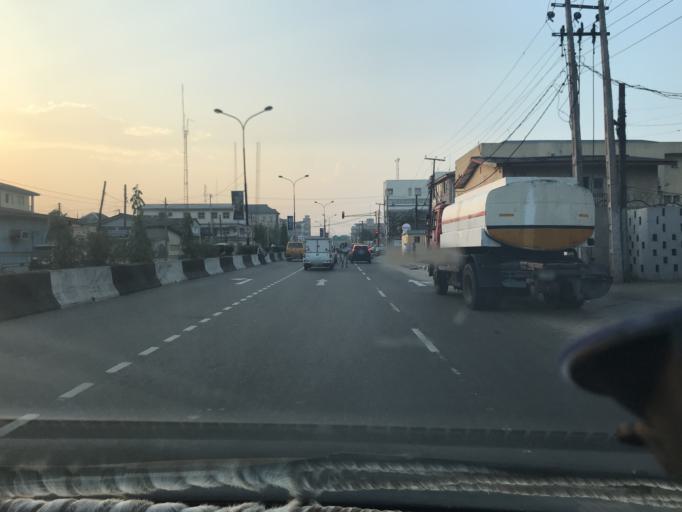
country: NG
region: Lagos
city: Makoko
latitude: 6.4958
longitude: 3.3805
